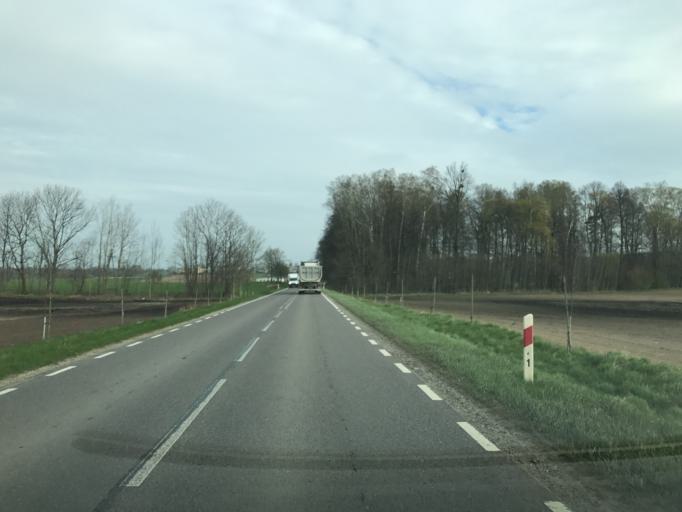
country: PL
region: Warmian-Masurian Voivodeship
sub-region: Powiat ostrodzki
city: Gierzwald
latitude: 53.5310
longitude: 20.0883
